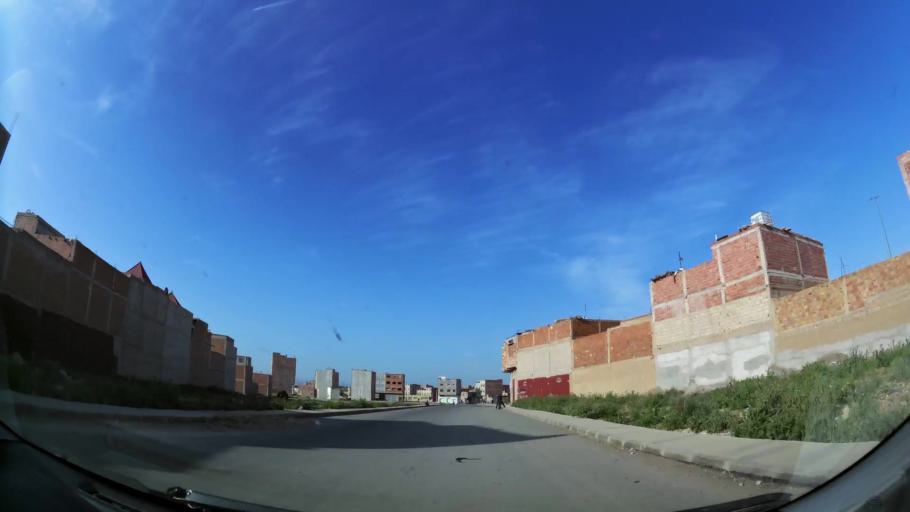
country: MA
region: Oriental
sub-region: Oujda-Angad
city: Oujda
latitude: 34.7165
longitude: -1.8991
